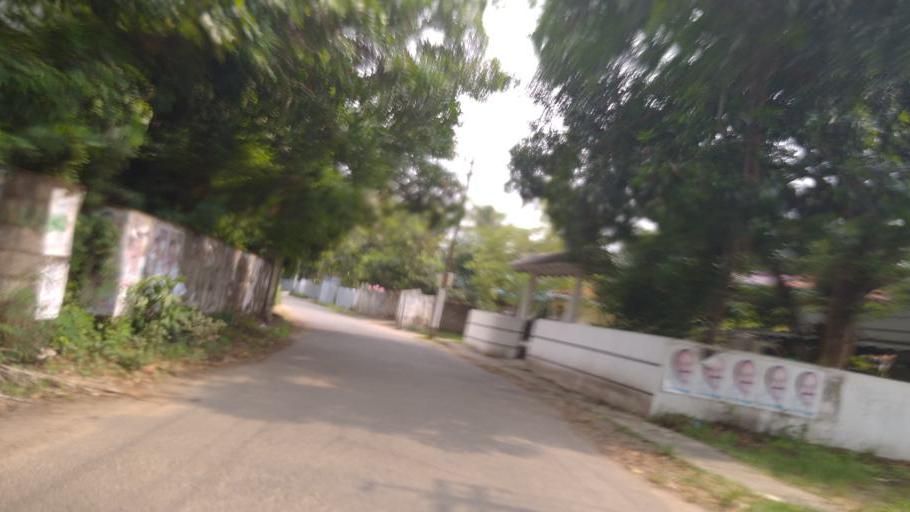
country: IN
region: Kerala
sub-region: Ernakulam
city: Elur
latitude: 10.1476
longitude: 76.2545
